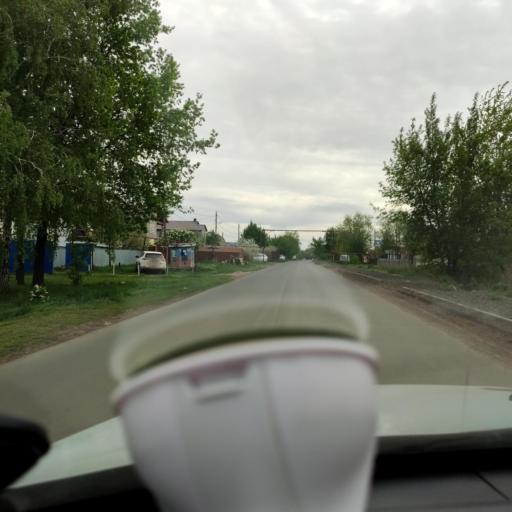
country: RU
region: Samara
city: Smyshlyayevka
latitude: 53.2216
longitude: 50.3374
